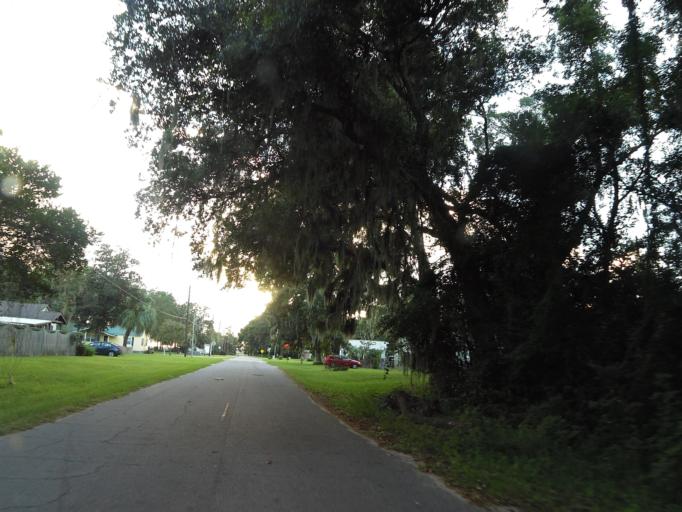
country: US
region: Georgia
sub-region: Camden County
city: St. Marys
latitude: 30.7335
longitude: -81.5553
